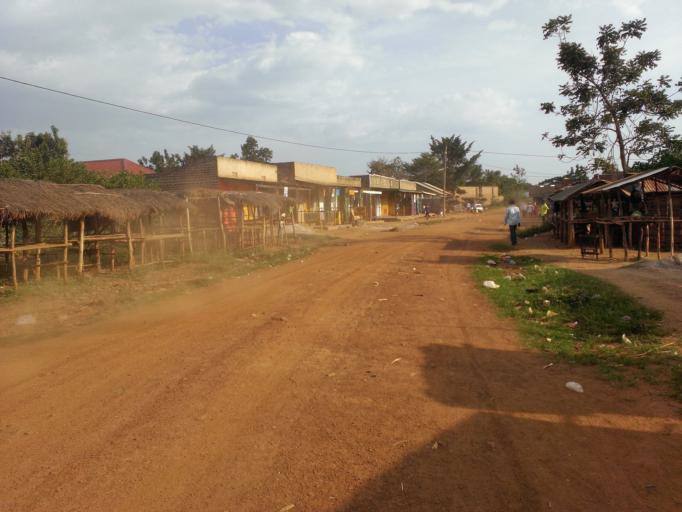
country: UG
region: Eastern Region
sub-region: Busia District
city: Busia
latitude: 0.5412
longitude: 34.0260
